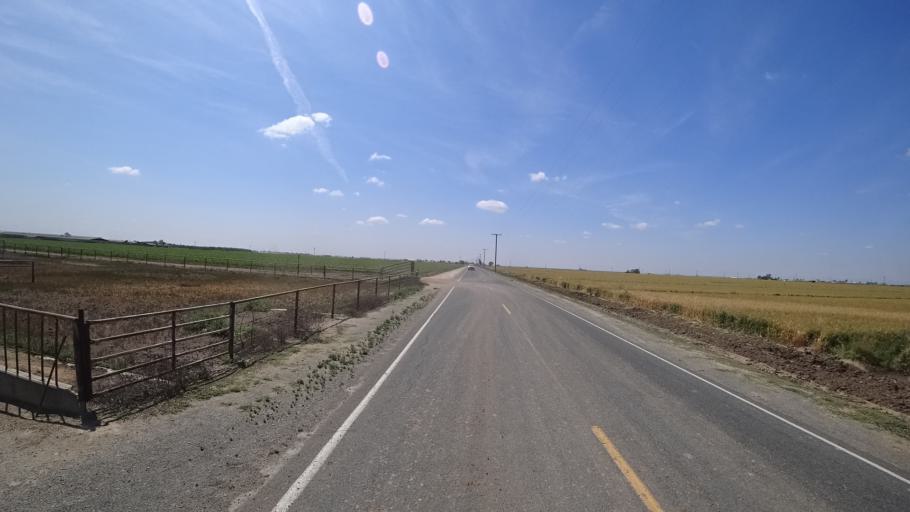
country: US
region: California
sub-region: Tulare County
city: Goshen
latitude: 36.3212
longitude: -119.4931
